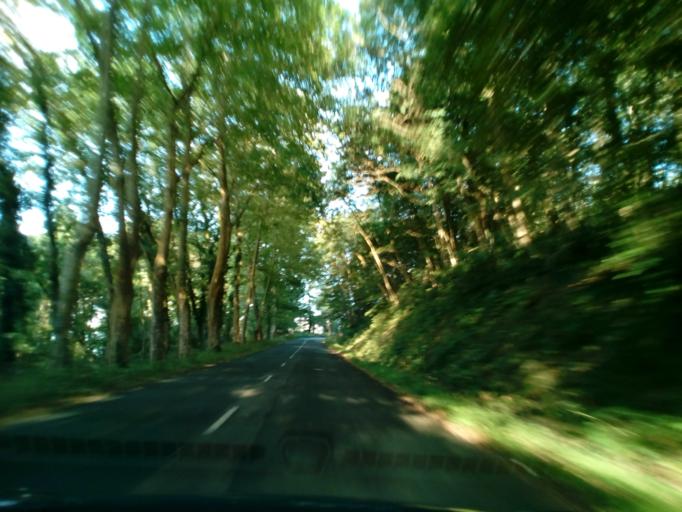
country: ES
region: Basque Country
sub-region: Provincia de Guipuzcoa
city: Urnieta
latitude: 43.2258
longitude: -1.9832
